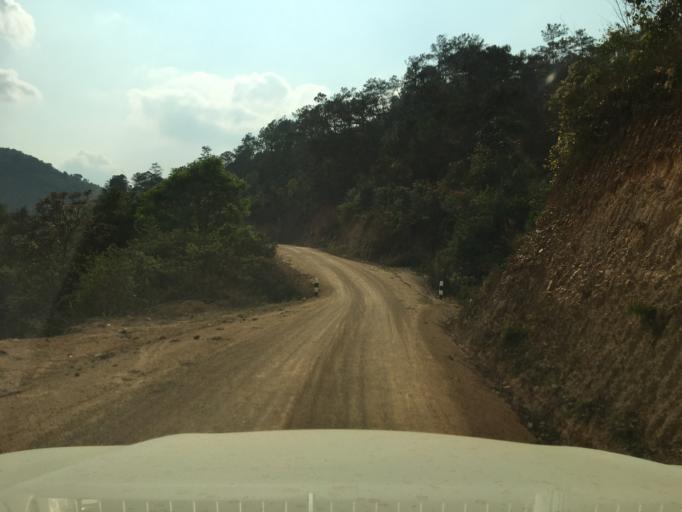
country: LA
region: Houaphan
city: Huameung
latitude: 20.2097
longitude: 103.8615
